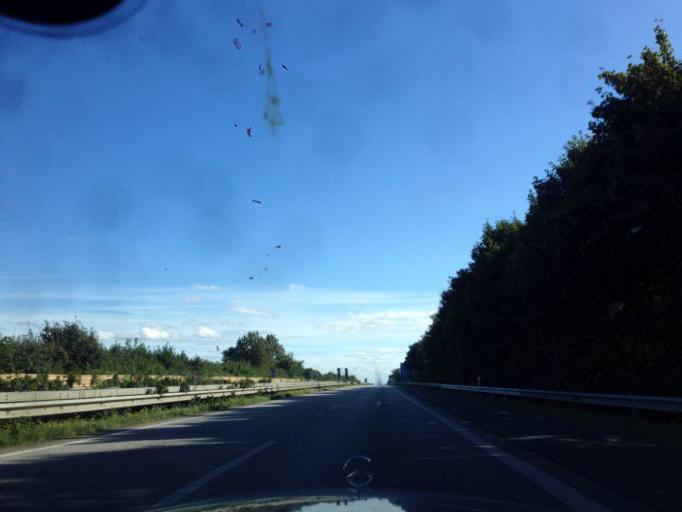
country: DE
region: Schleswig-Holstein
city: Jarplund-Weding
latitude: 54.7439
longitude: 9.3801
